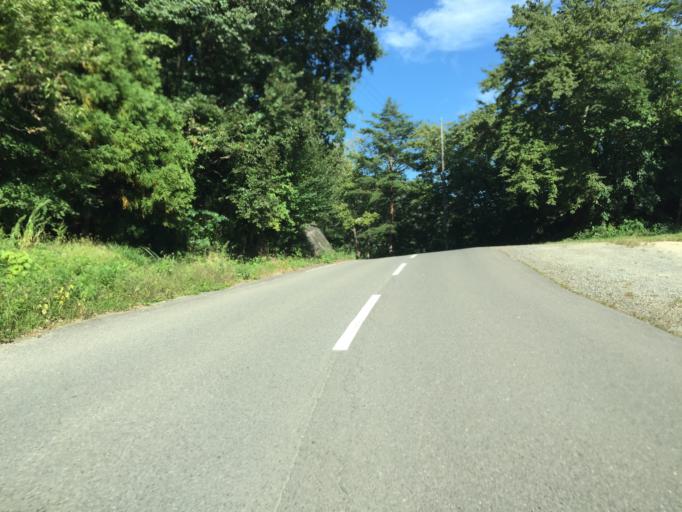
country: JP
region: Miyagi
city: Marumori
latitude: 37.8707
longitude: 140.7820
